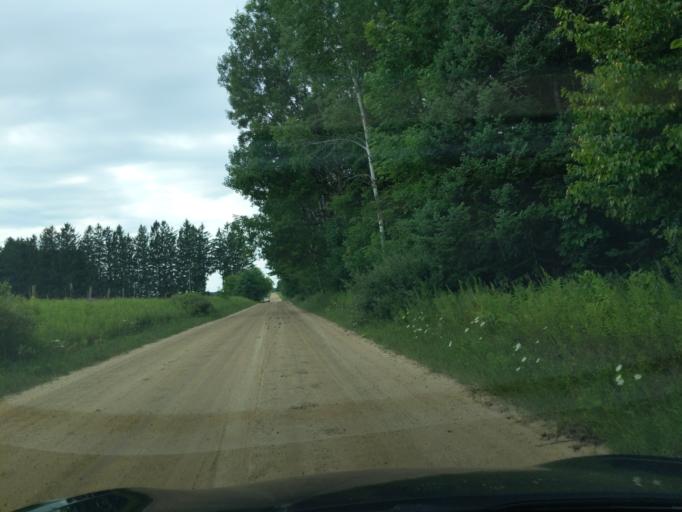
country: US
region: Michigan
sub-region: Clare County
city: Harrison
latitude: 44.0025
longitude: -84.9808
